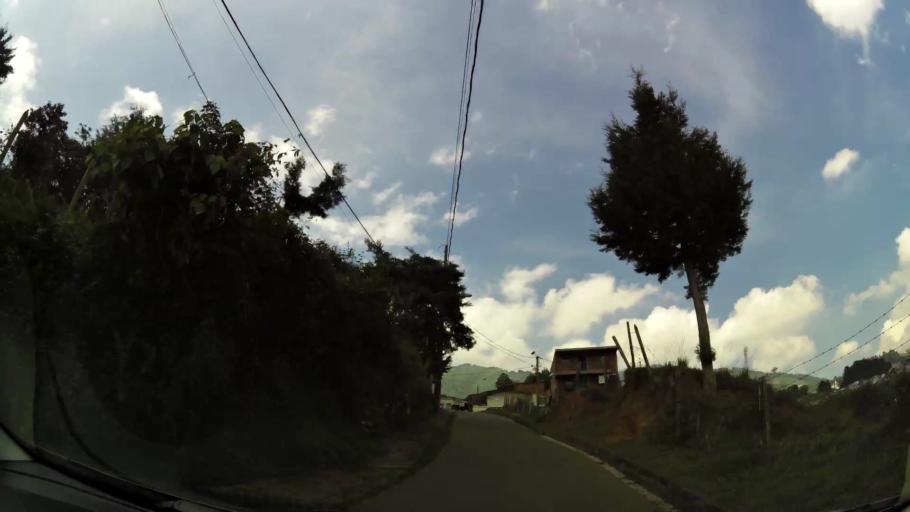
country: CO
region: Antioquia
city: La Estrella
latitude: 6.1728
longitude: -75.6541
